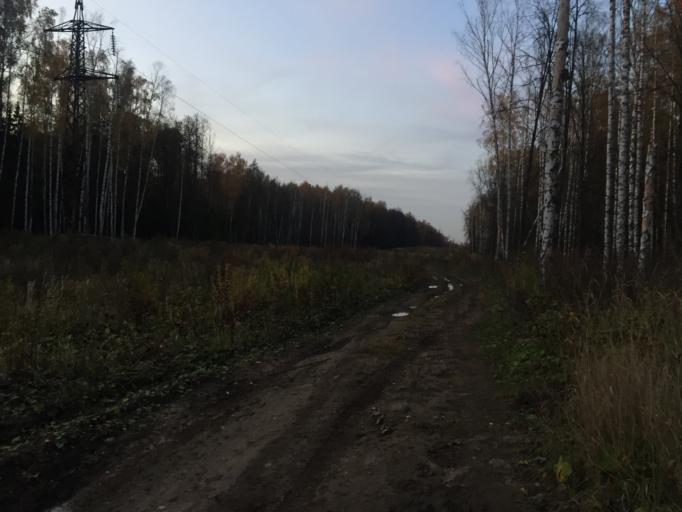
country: RU
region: Moskovskaya
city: Druzhba
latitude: 55.8715
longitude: 37.7674
